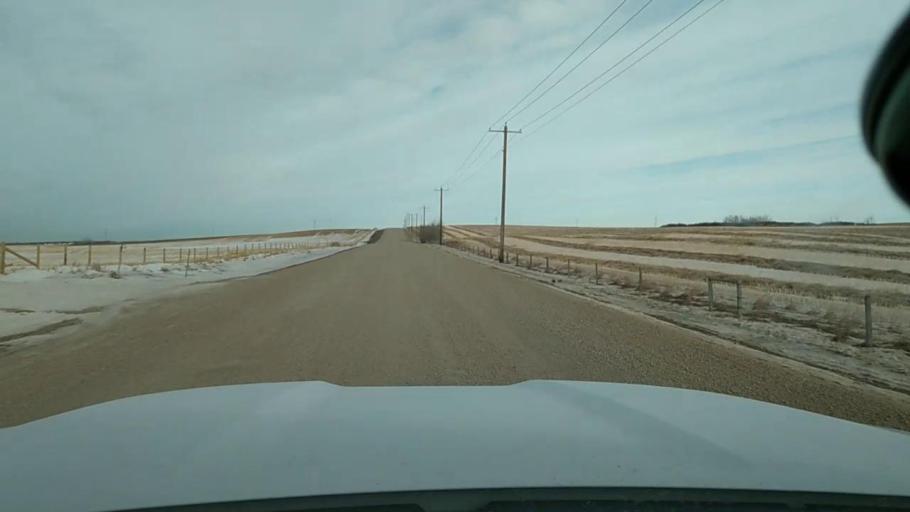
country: CA
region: Alberta
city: Airdrie
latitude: 51.2359
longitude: -113.9118
